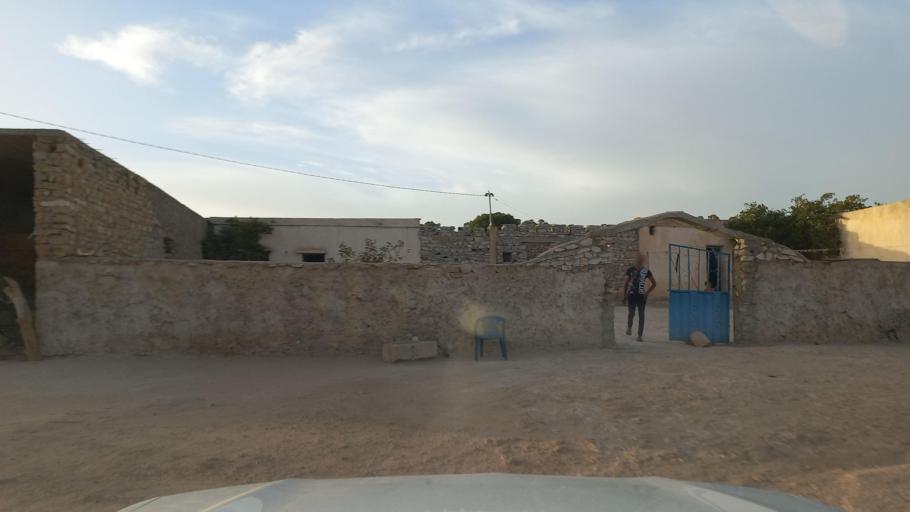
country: TN
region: Al Qasrayn
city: Sbiba
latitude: 35.4130
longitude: 8.9136
